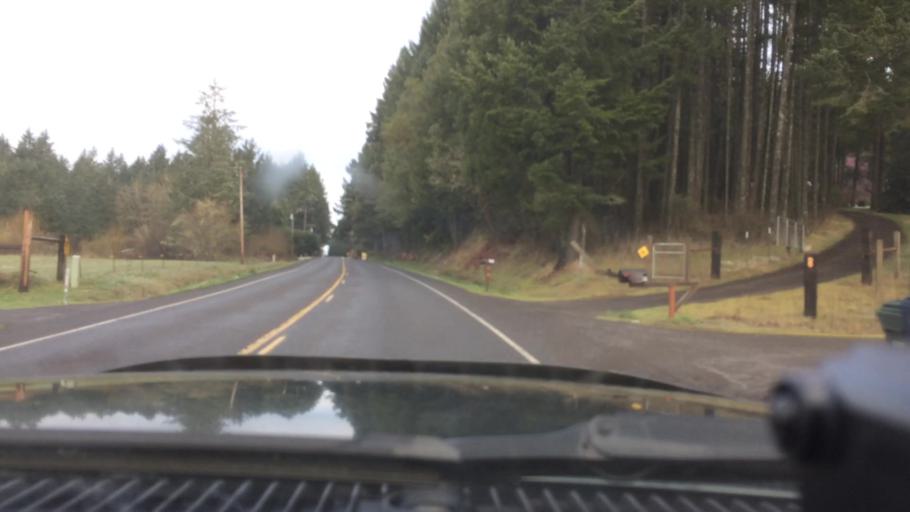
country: US
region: Oregon
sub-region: Lane County
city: Veneta
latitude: 44.1341
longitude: -123.3495
